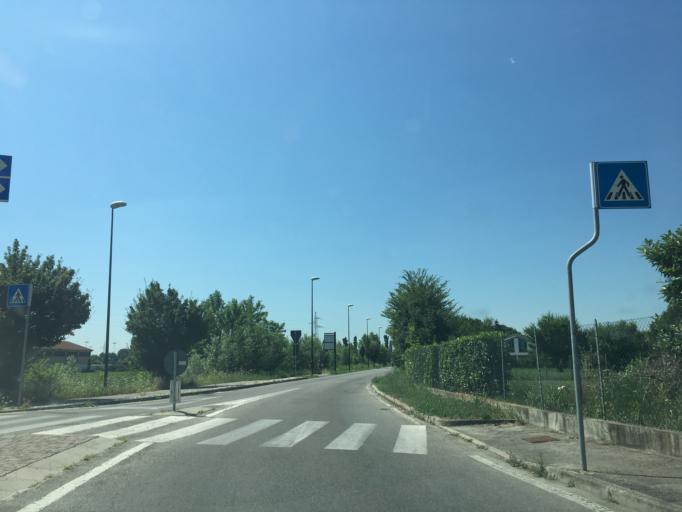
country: IT
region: Veneto
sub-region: Provincia di Venezia
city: Zelarino
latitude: 45.4947
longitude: 12.1917
